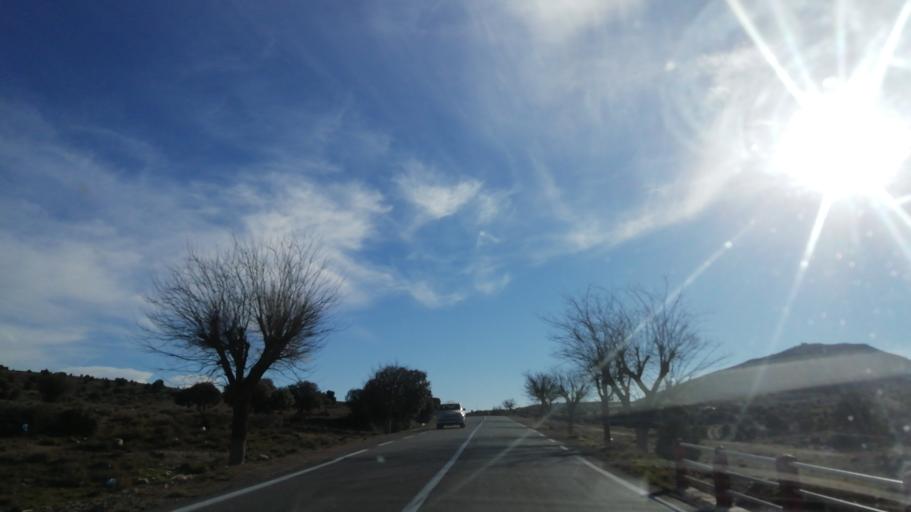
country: DZ
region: Tlemcen
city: Sebdou
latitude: 34.5794
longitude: -1.3191
